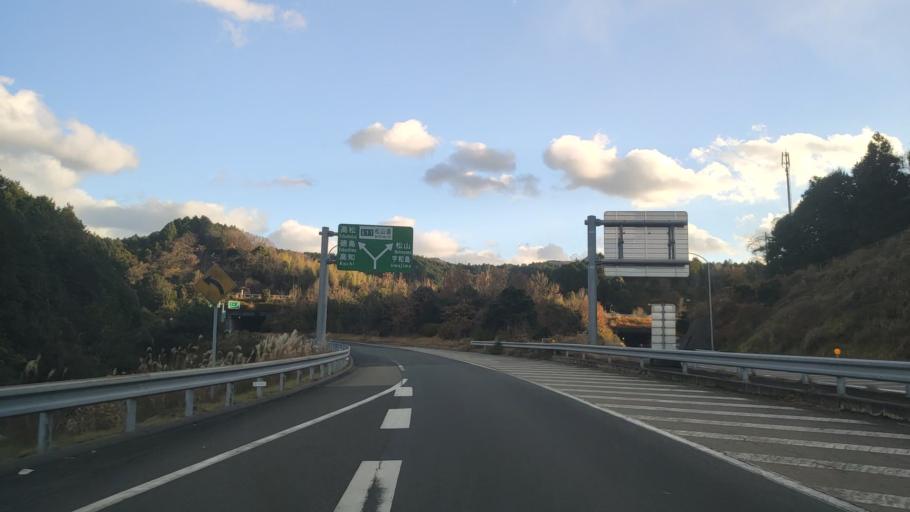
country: JP
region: Ehime
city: Saijo
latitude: 33.8845
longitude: 133.0884
